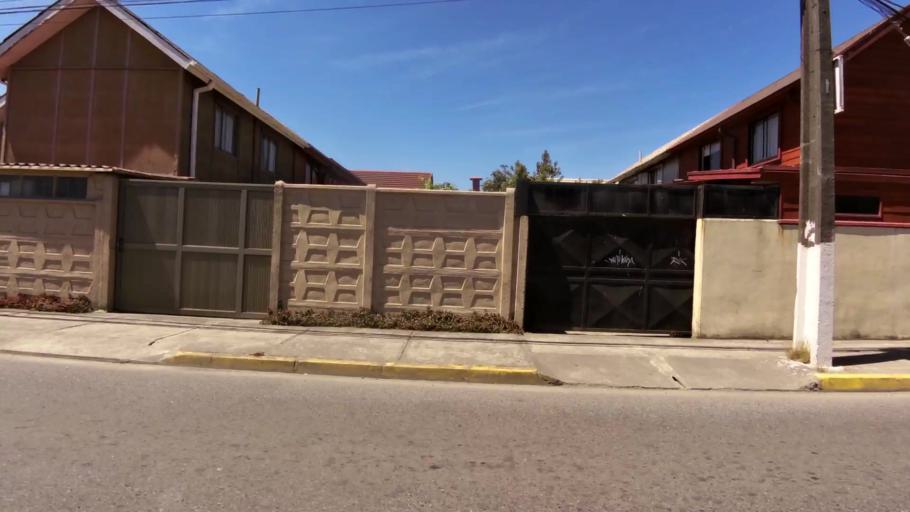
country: CL
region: Biobio
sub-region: Provincia de Concepcion
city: Talcahuano
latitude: -36.7593
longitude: -73.0840
